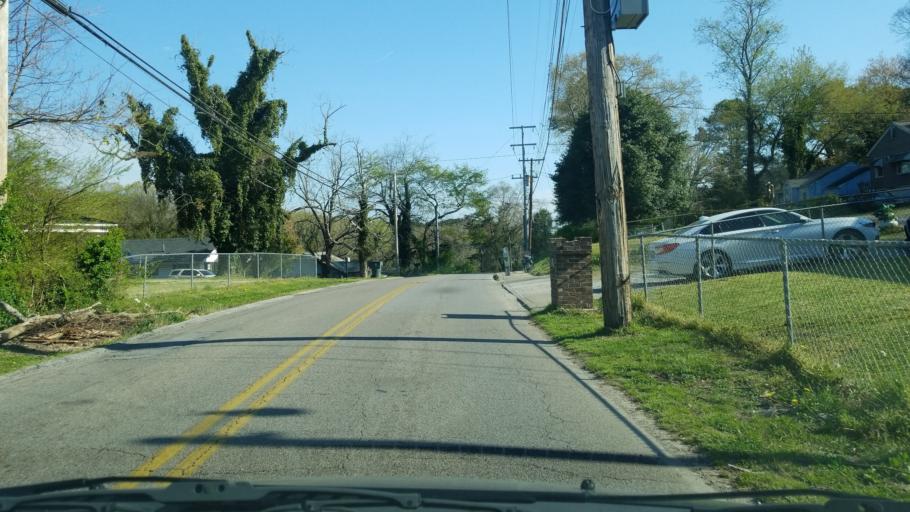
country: US
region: Tennessee
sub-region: Hamilton County
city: East Chattanooga
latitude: 35.0495
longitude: -85.2361
